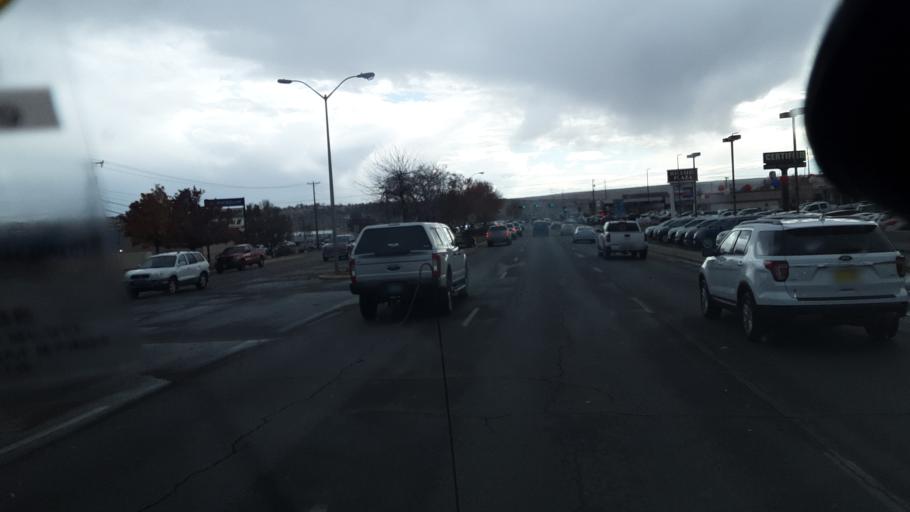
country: US
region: New Mexico
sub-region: San Juan County
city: Farmington
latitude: 36.7607
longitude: -108.1558
